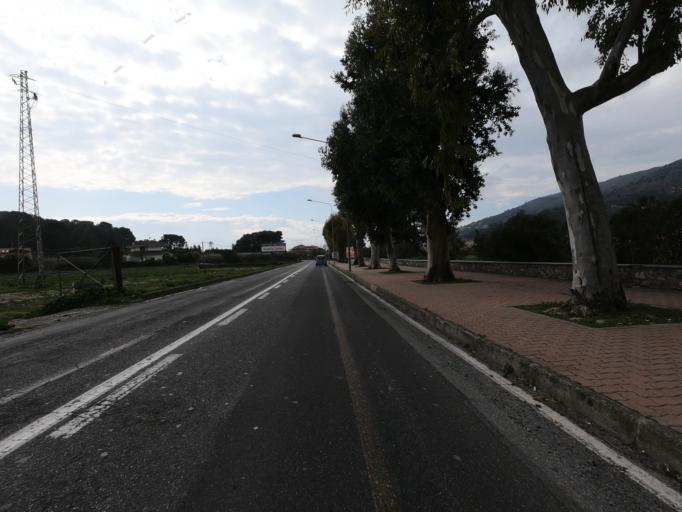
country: IT
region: Liguria
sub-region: Provincia di Savona
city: Andora
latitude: 43.9643
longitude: 8.1418
